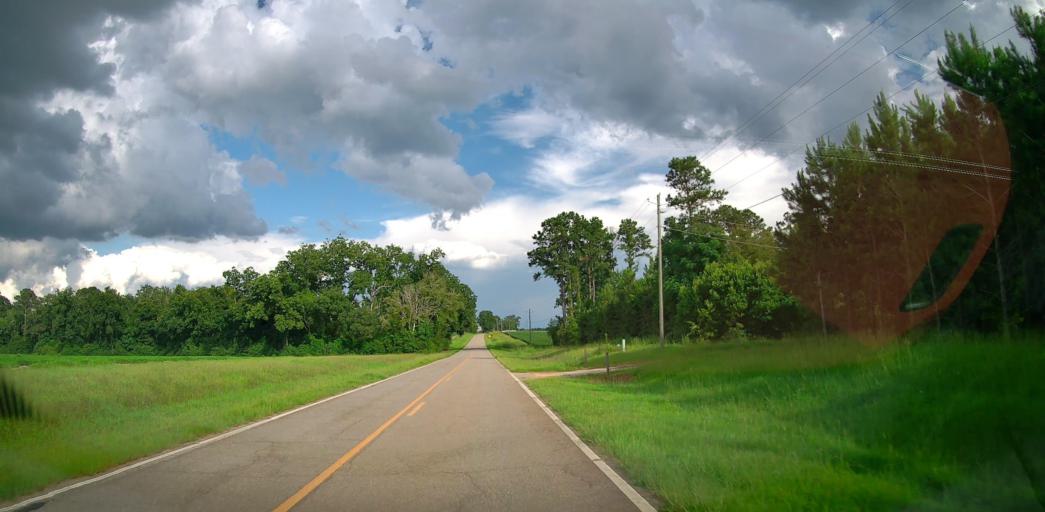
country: US
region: Georgia
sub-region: Bleckley County
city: Cochran
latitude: 32.4044
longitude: -83.3798
